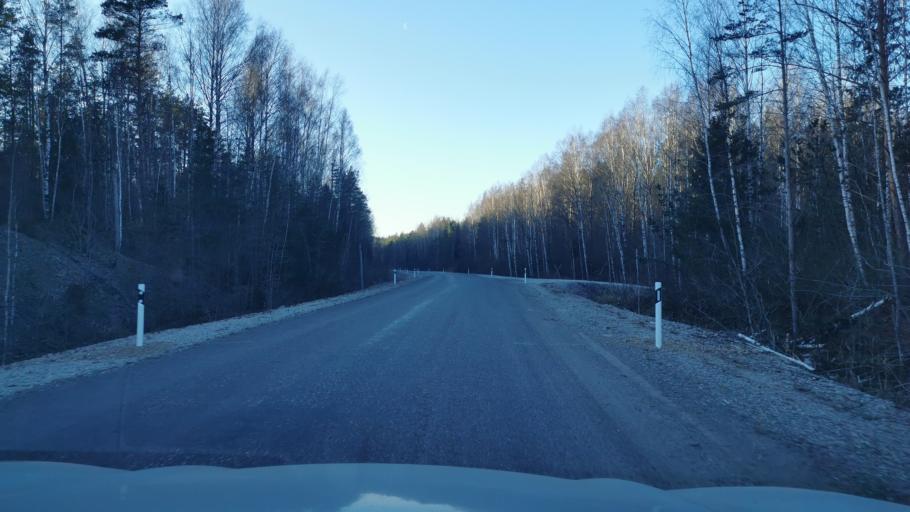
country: EE
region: Ida-Virumaa
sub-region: Kohtla-Nomme vald
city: Kohtla-Nomme
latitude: 59.3492
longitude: 27.1599
